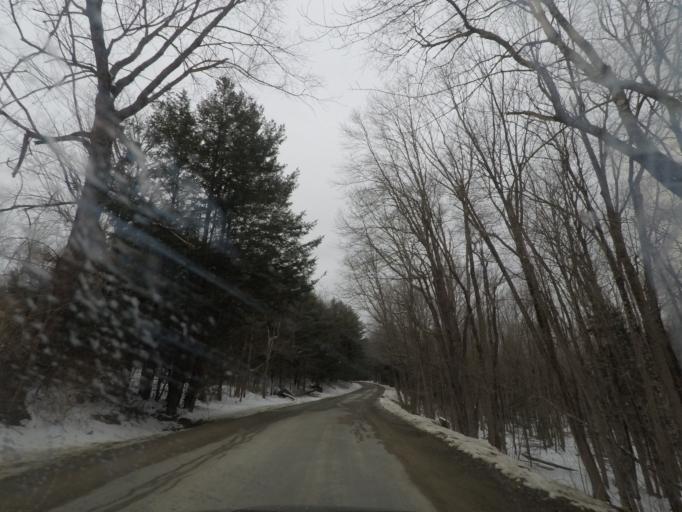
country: US
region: New York
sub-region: Rensselaer County
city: Averill Park
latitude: 42.5475
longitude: -73.4130
